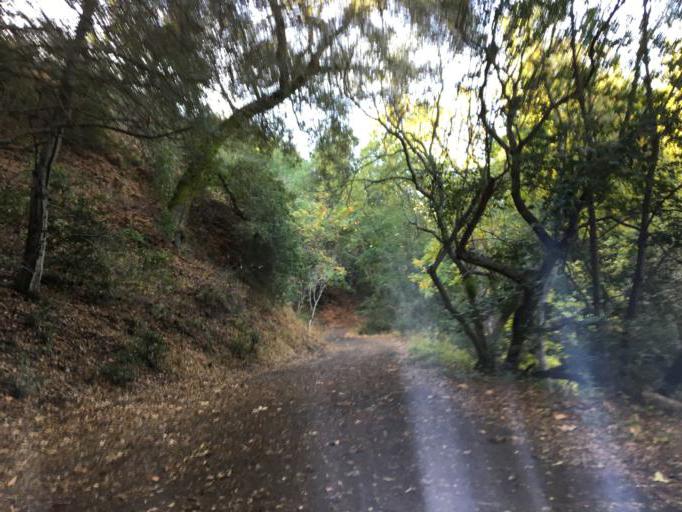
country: US
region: California
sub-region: Santa Clara County
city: Cupertino
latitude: 37.3040
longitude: -122.0739
